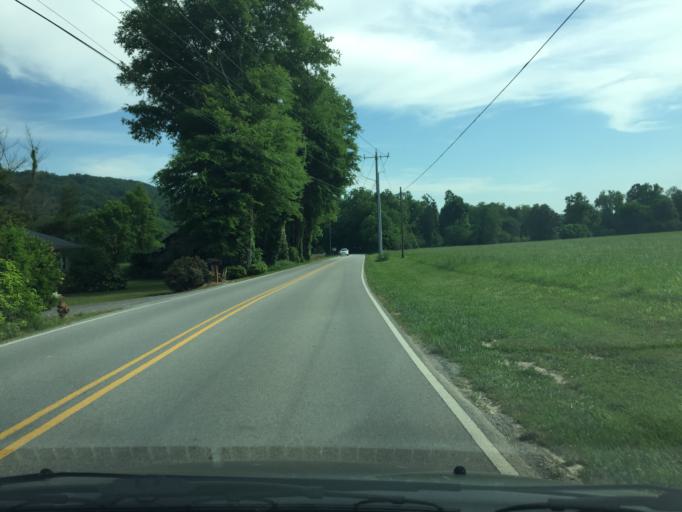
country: US
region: Tennessee
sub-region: Hamilton County
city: Collegedale
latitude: 35.0756
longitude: -85.0336
